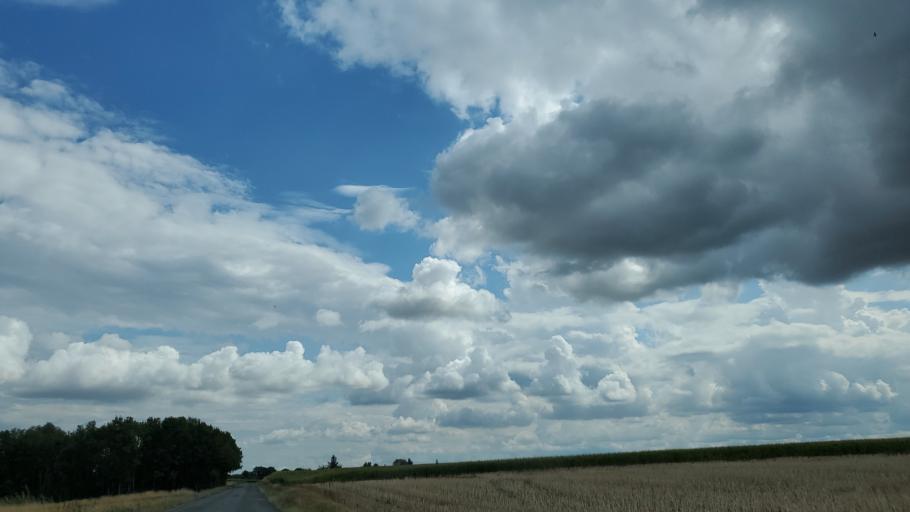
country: FR
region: Ile-de-France
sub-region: Departement de Seine-et-Marne
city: Mouroux
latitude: 48.8383
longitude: 3.0316
